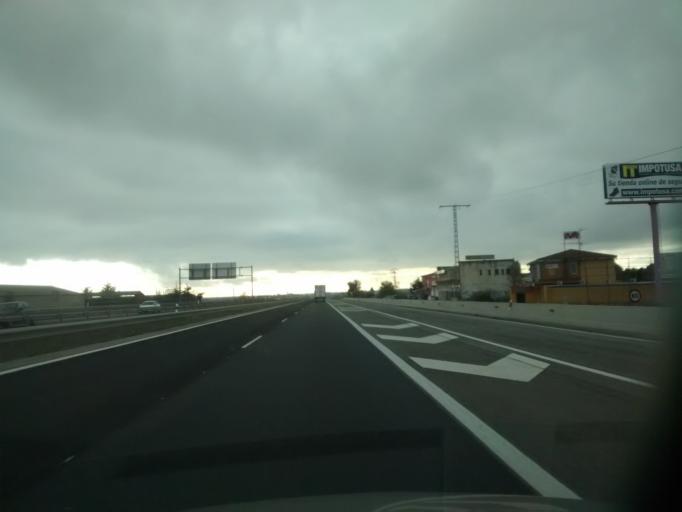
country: ES
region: Castille-La Mancha
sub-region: Provincia de Guadalajara
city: Trijueque
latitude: 40.7754
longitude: -2.9925
